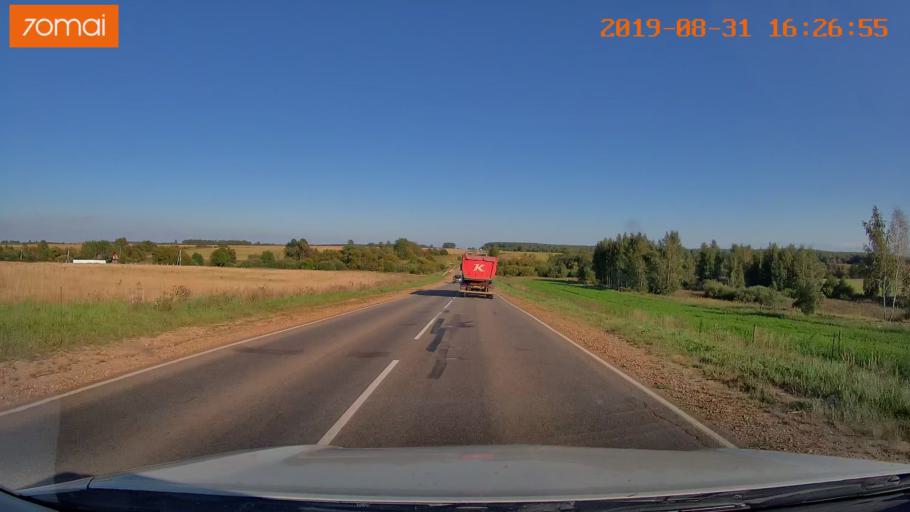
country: RU
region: Kaluga
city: Babynino
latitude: 54.5151
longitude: 35.7439
